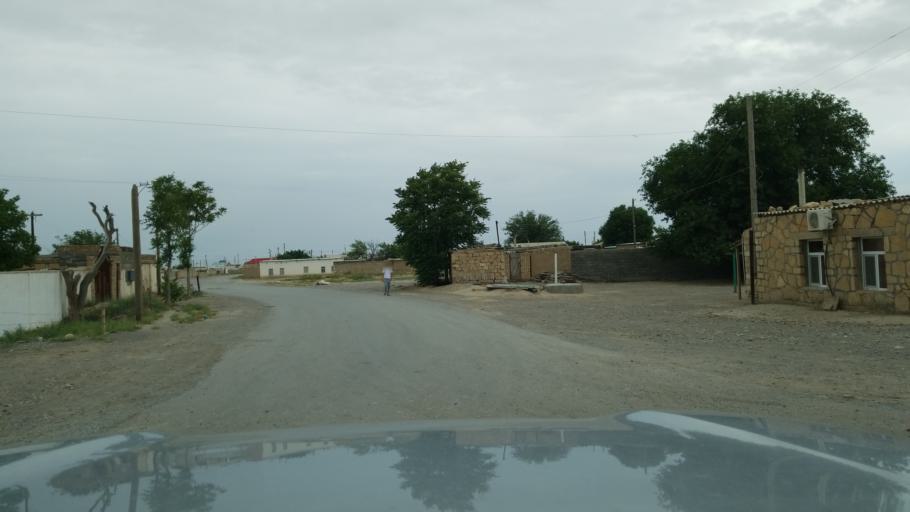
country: TM
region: Balkan
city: Serdar
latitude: 38.9885
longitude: 56.2773
